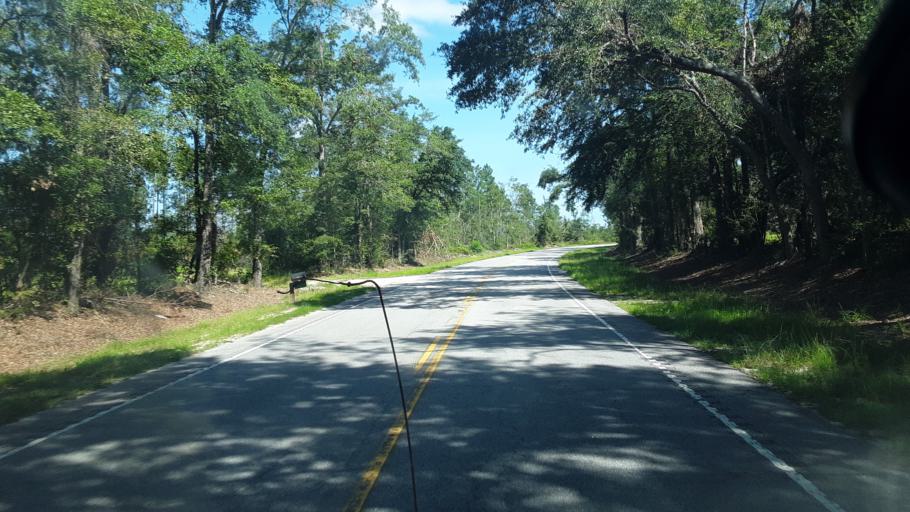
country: US
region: South Carolina
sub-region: Hampton County
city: Varnville
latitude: 32.7896
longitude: -81.0590
